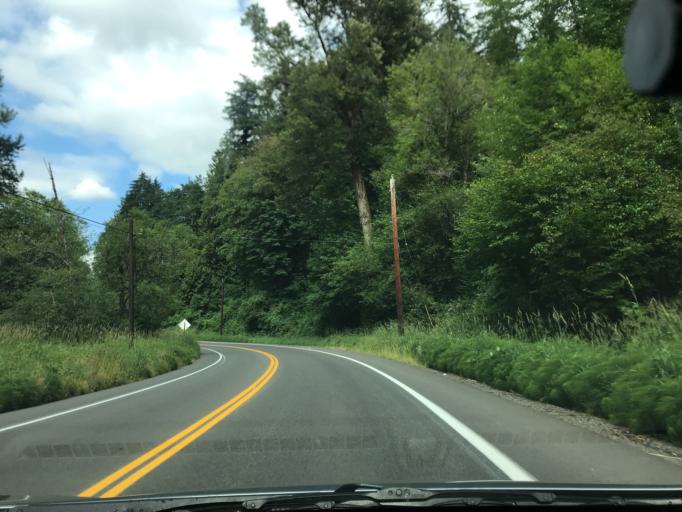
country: US
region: Washington
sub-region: King County
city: Lea Hill
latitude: 47.3136
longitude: -122.1621
